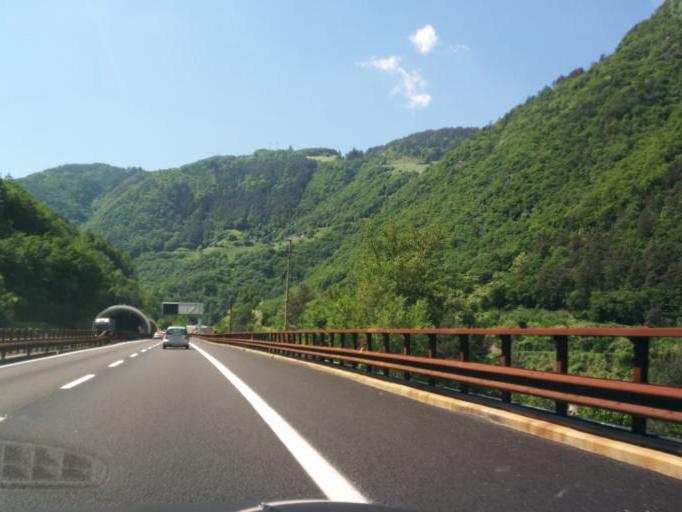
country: IT
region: Trentino-Alto Adige
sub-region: Bolzano
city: Ponte Gardena
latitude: 46.5639
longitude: 11.5165
